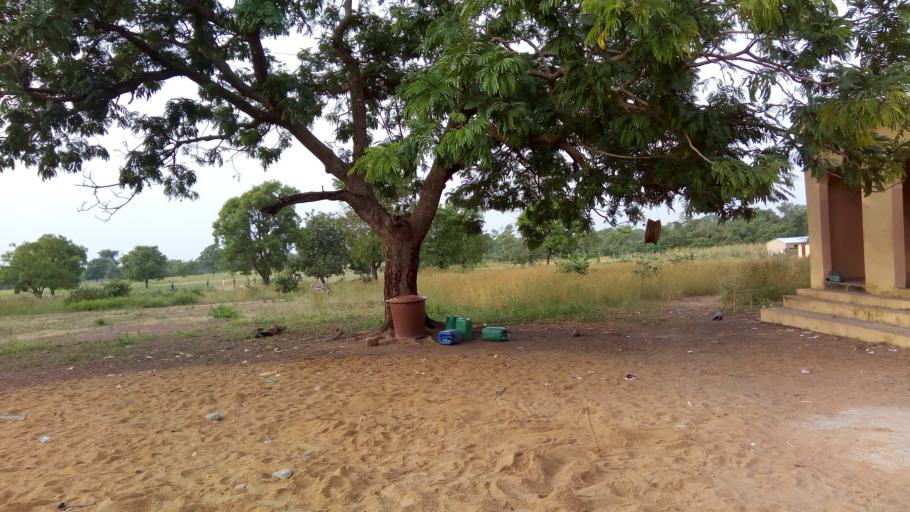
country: ML
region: Koulikoro
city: Kangaba
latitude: 11.6776
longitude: -8.6513
